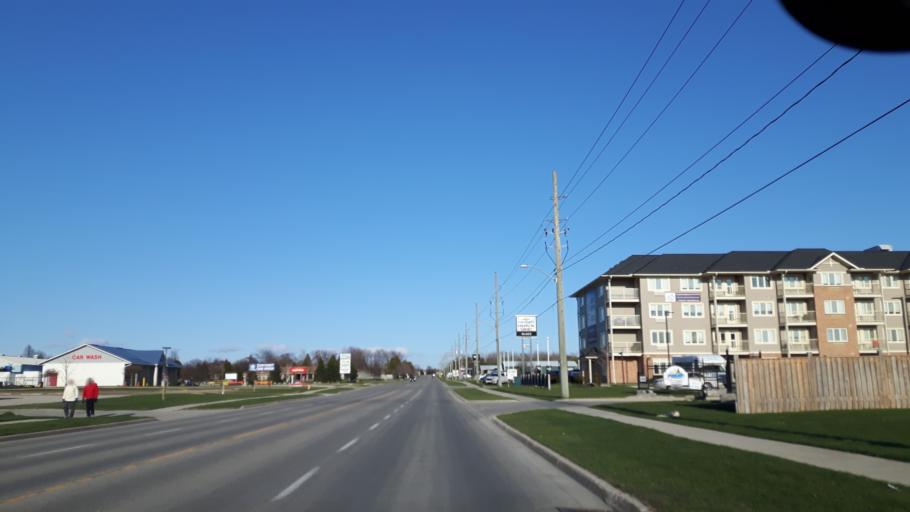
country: CA
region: Ontario
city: Goderich
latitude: 43.7316
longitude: -81.7053
